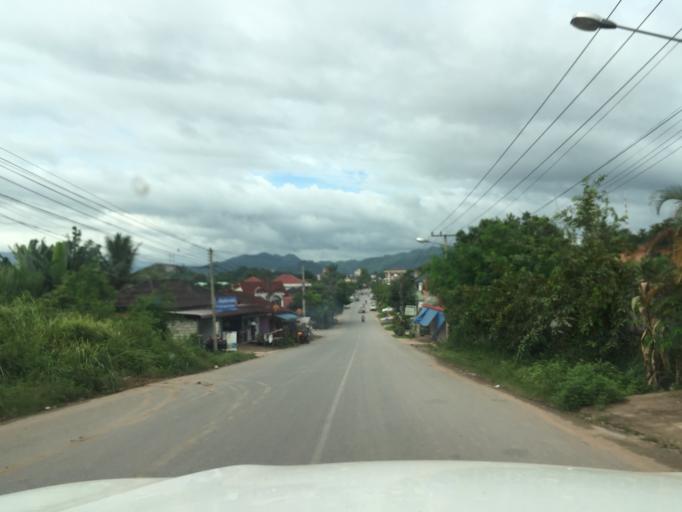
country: LA
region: Oudomxai
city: Muang Xay
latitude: 20.7016
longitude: 101.9937
